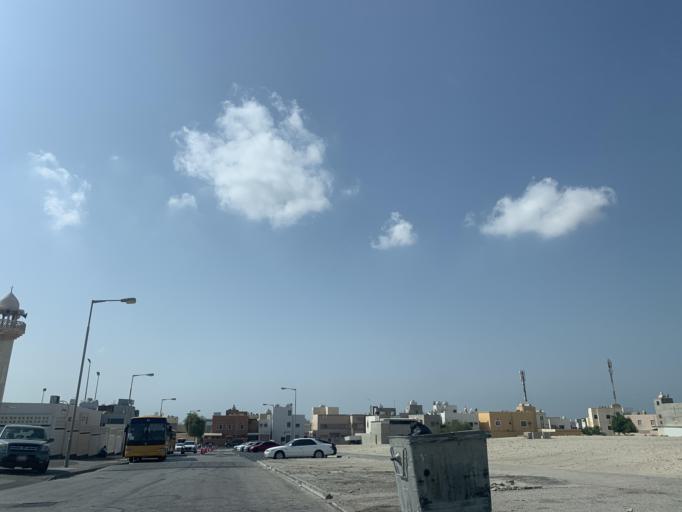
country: BH
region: Central Governorate
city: Madinat Hamad
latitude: 26.1360
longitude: 50.5049
